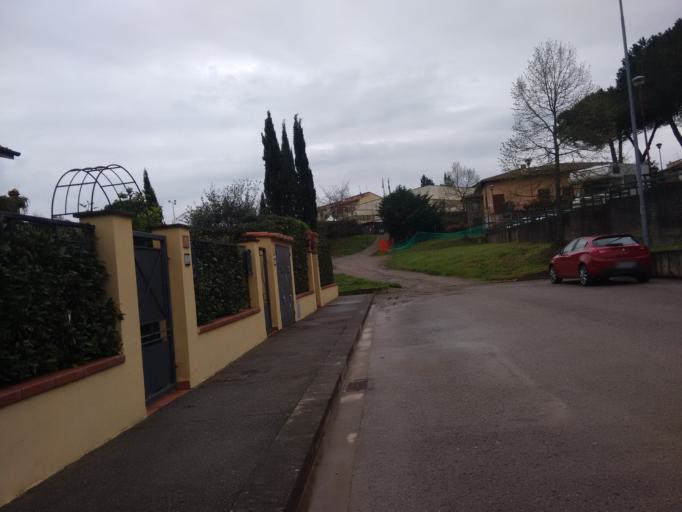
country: IT
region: Tuscany
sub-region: Province of Florence
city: Strada in Chianti
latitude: 43.6574
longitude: 11.3009
